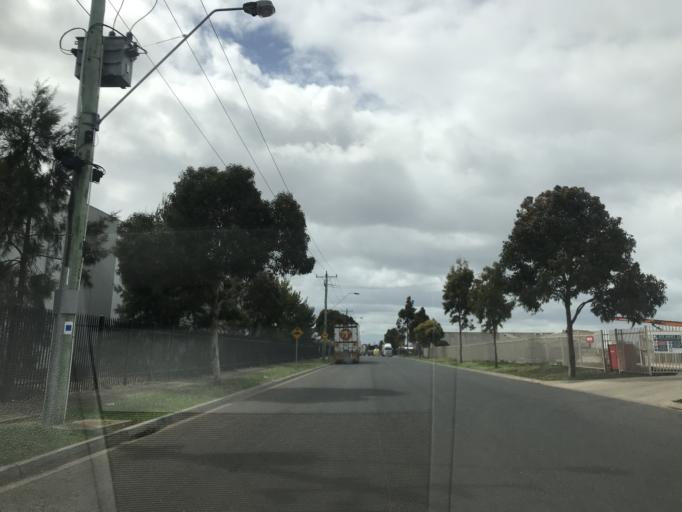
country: AU
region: Victoria
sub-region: Brimbank
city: Derrimut
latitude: -37.7915
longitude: 144.7758
